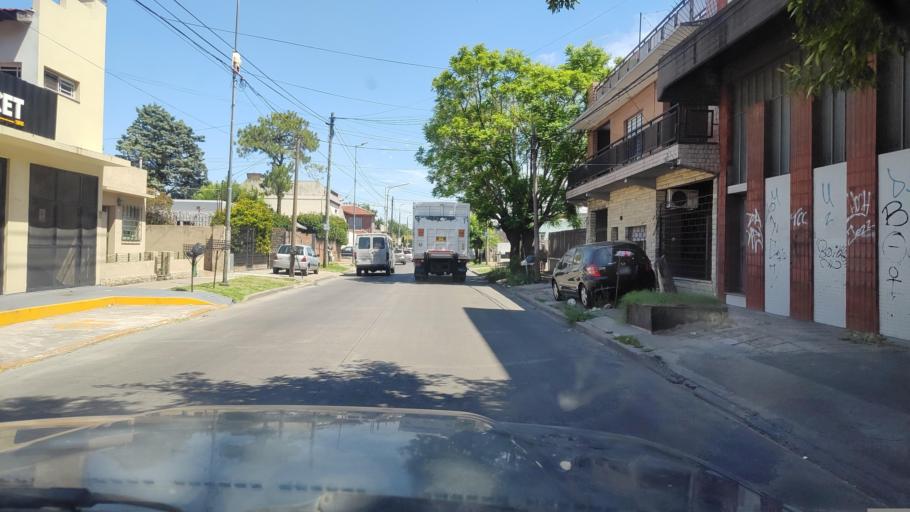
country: AR
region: Buenos Aires
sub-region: Partido de Moron
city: Moron
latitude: -34.6640
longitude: -58.6015
